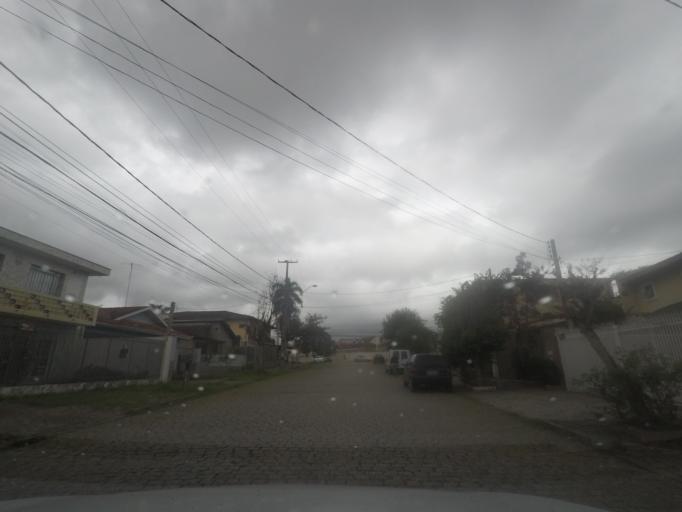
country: BR
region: Parana
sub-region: Curitiba
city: Curitiba
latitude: -25.4387
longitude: -49.2464
